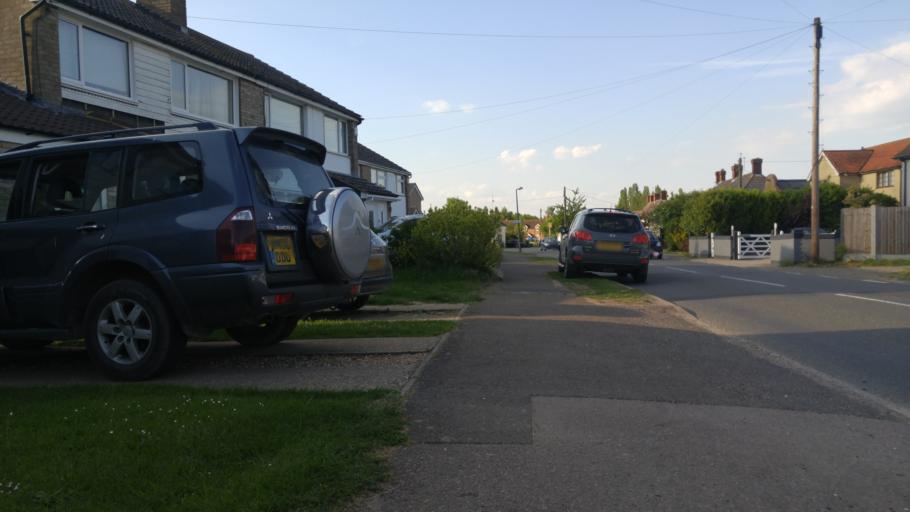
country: GB
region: England
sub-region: Essex
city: Eight Ash Green
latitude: 51.9220
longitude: 0.8034
